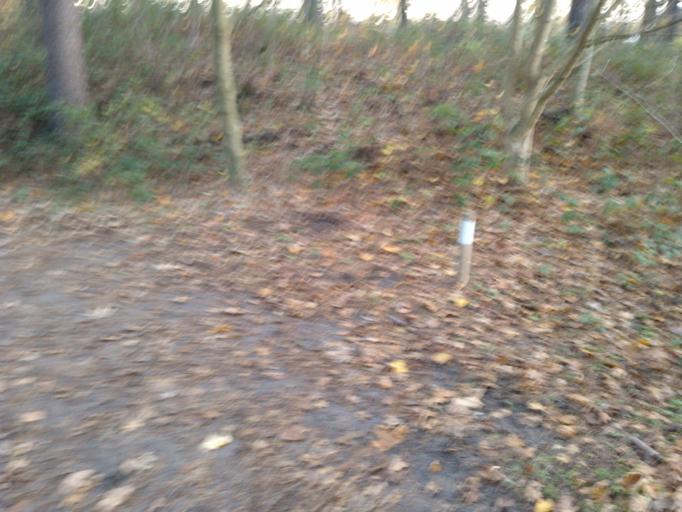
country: NL
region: South Holland
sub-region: Gemeente Noordwijkerhout
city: Noordwijkerhout
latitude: 52.2774
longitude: 4.4762
